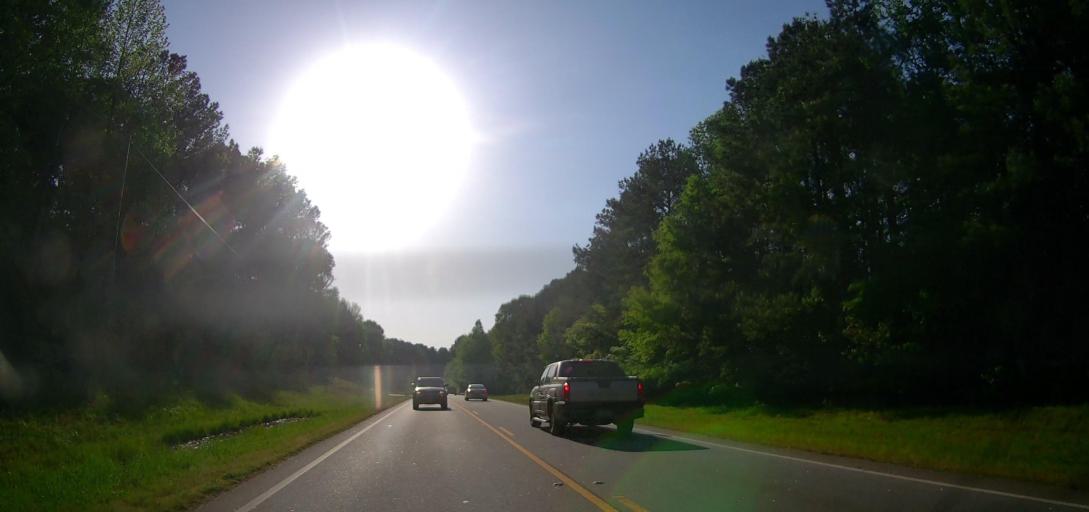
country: US
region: Georgia
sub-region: Newton County
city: Porterdale
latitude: 33.5573
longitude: -83.8920
